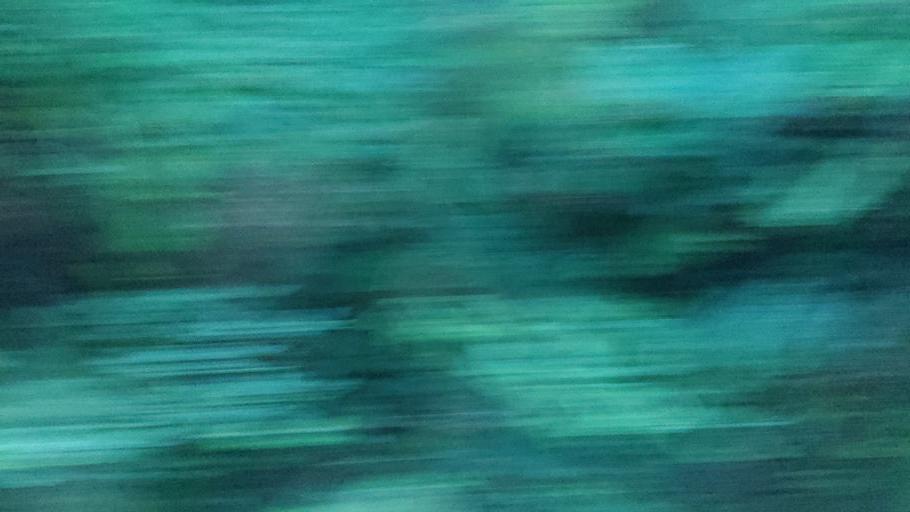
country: TW
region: Taiwan
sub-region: Yunlin
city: Douliu
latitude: 23.5311
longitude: 120.6504
